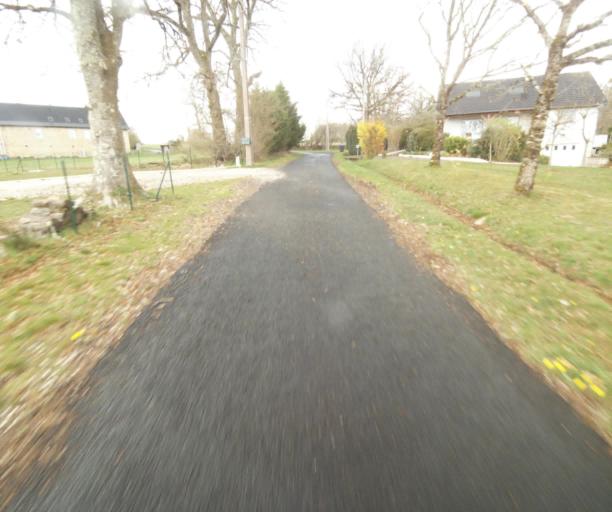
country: FR
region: Limousin
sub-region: Departement de la Correze
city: Egletons
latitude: 45.2569
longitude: 1.9959
